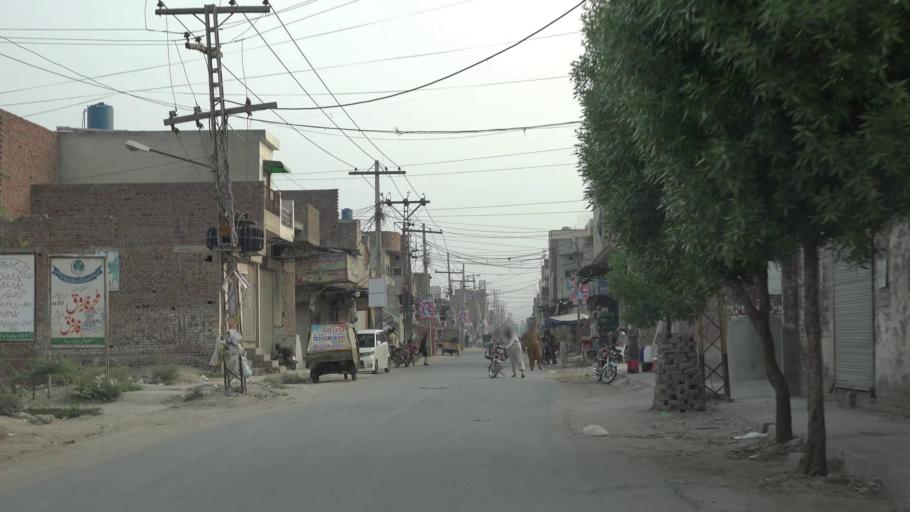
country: PK
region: Punjab
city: Faisalabad
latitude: 31.4316
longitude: 73.1419
